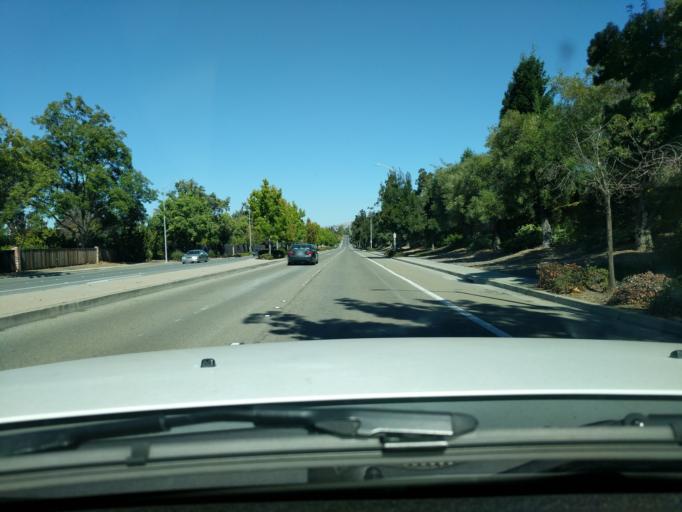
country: US
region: California
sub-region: Santa Clara County
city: Milpitas
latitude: 37.5024
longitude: -121.9195
